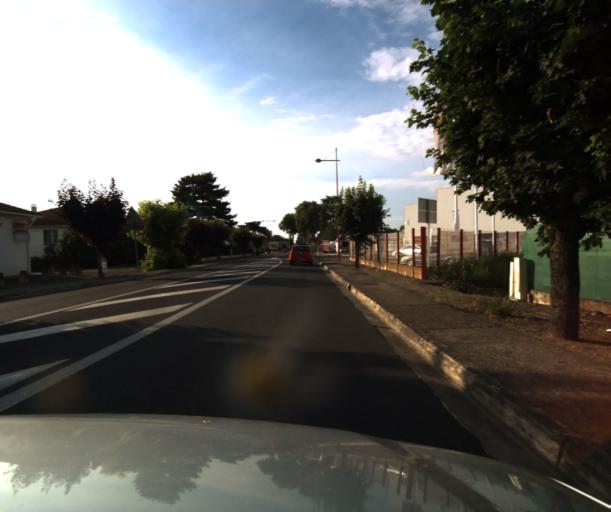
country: FR
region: Midi-Pyrenees
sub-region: Departement du Tarn-et-Garonne
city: Castelsarrasin
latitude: 44.0475
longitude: 1.1030
